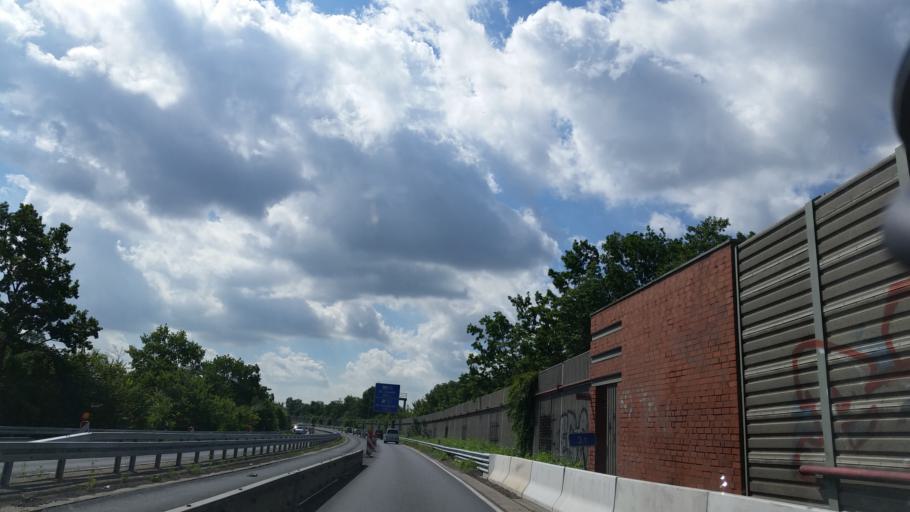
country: DE
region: Lower Saxony
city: Braunschweig
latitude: 52.2530
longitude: 10.4951
